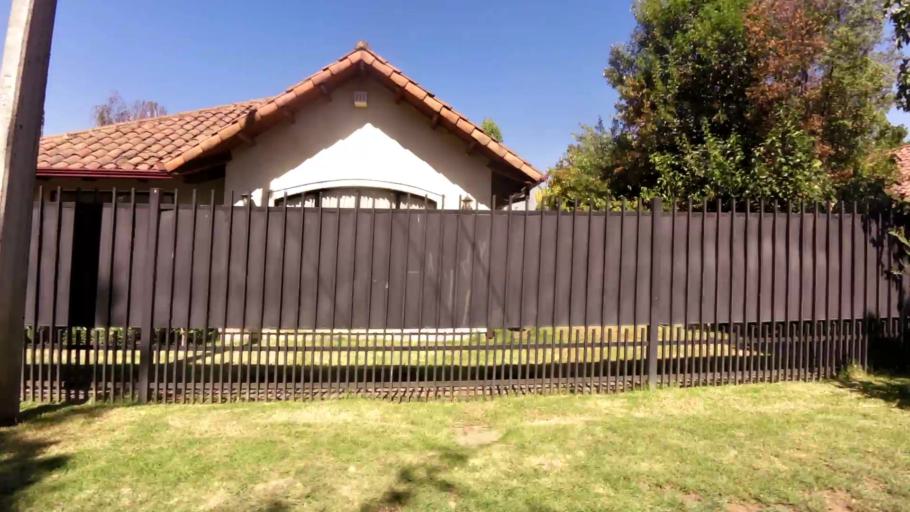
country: CL
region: Maule
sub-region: Provincia de Talca
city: Talca
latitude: -35.4318
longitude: -71.6165
